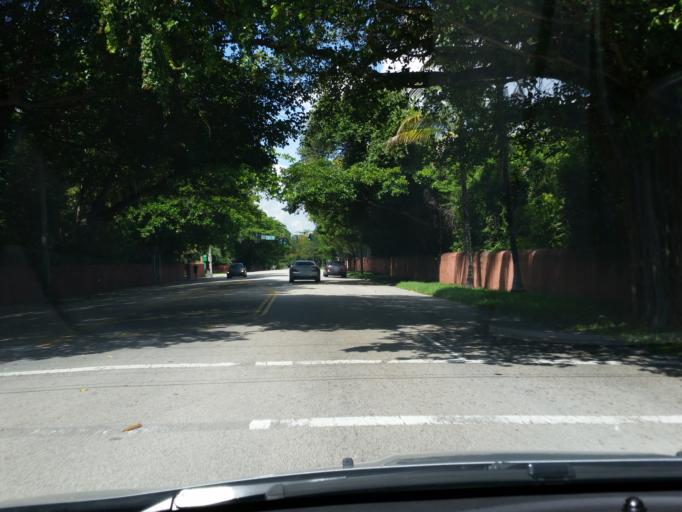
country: US
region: Florida
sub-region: Miami-Dade County
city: Miami
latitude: 25.7438
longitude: -80.2157
